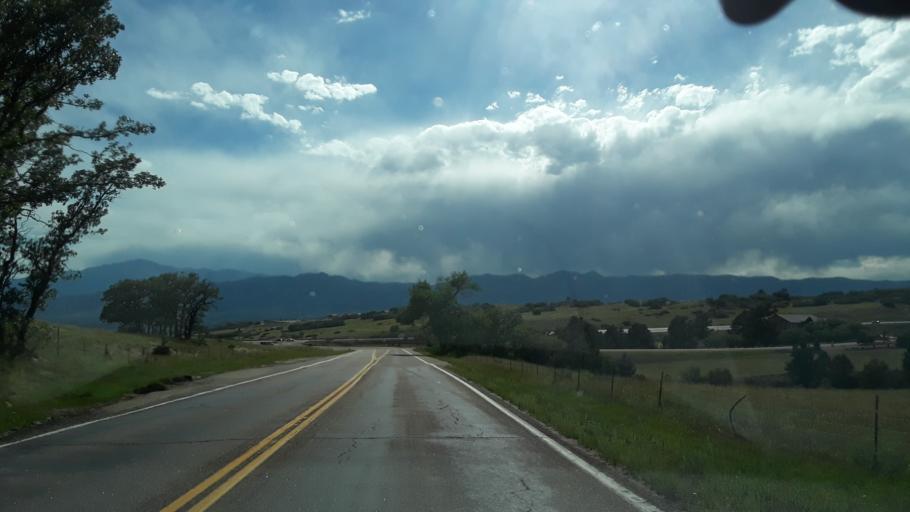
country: US
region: Colorado
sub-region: El Paso County
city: Gleneagle
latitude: 39.0113
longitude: -104.7740
